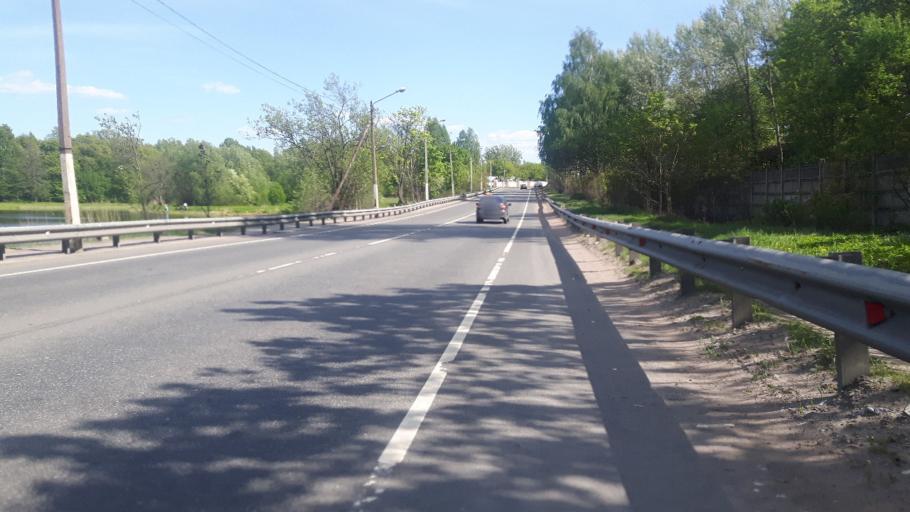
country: RU
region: Leningrad
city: Vyborg
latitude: 60.7234
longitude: 28.7132
